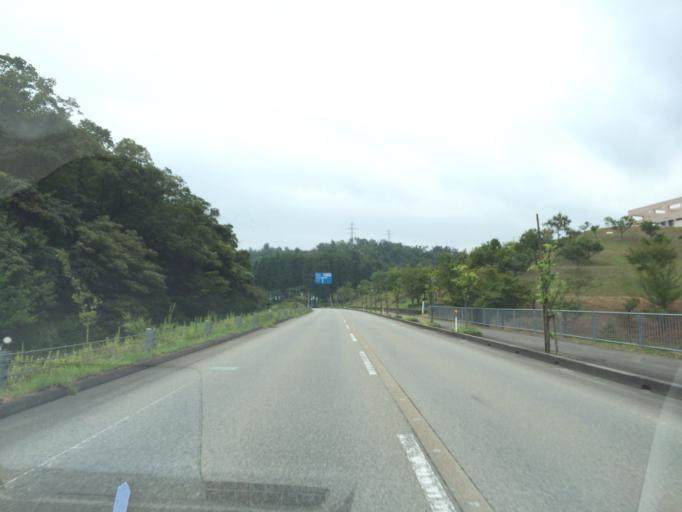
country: JP
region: Hyogo
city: Toyooka
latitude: 35.5284
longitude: 134.8087
